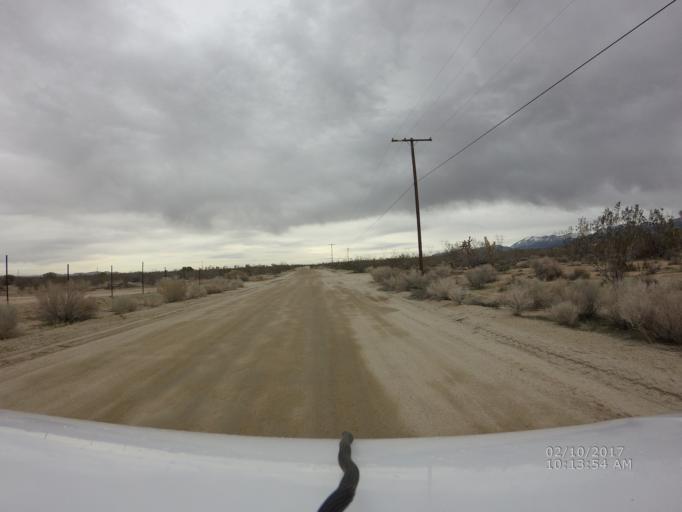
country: US
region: California
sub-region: Los Angeles County
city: Littlerock
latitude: 34.5139
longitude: -117.9765
